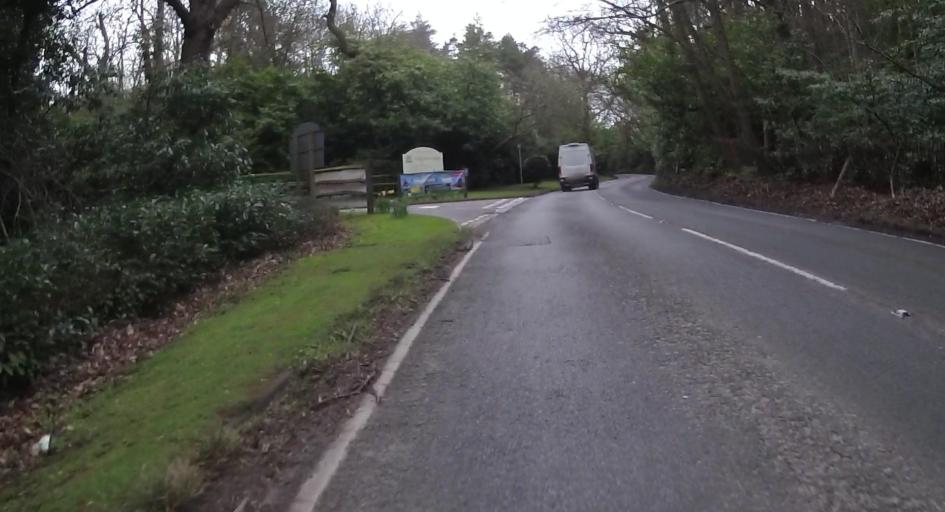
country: GB
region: England
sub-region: Surrey
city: Farnham
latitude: 51.1833
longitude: -0.7914
